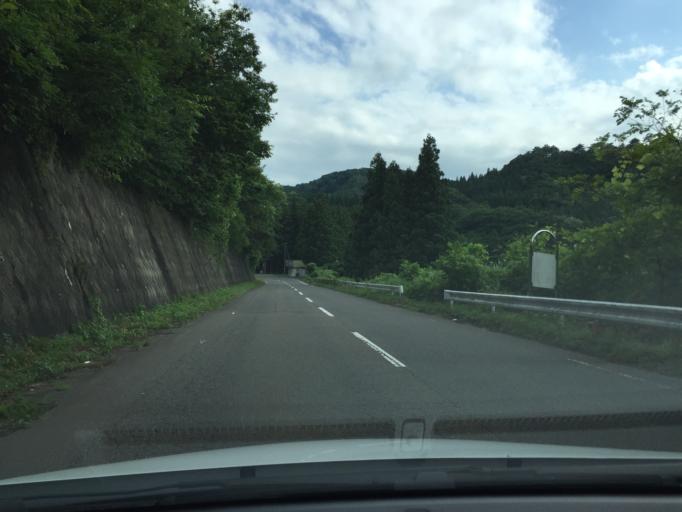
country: JP
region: Tochigi
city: Kuroiso
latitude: 37.1957
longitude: 140.1275
